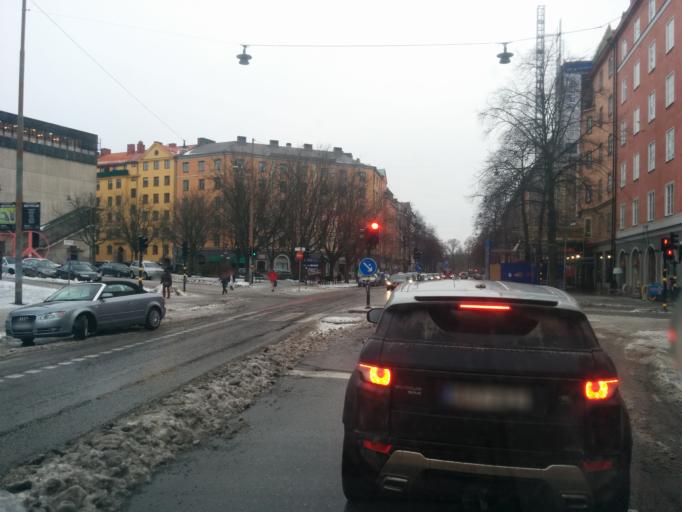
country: SE
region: Stockholm
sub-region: Stockholms Kommun
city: Stockholm
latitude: 59.3434
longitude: 18.0671
